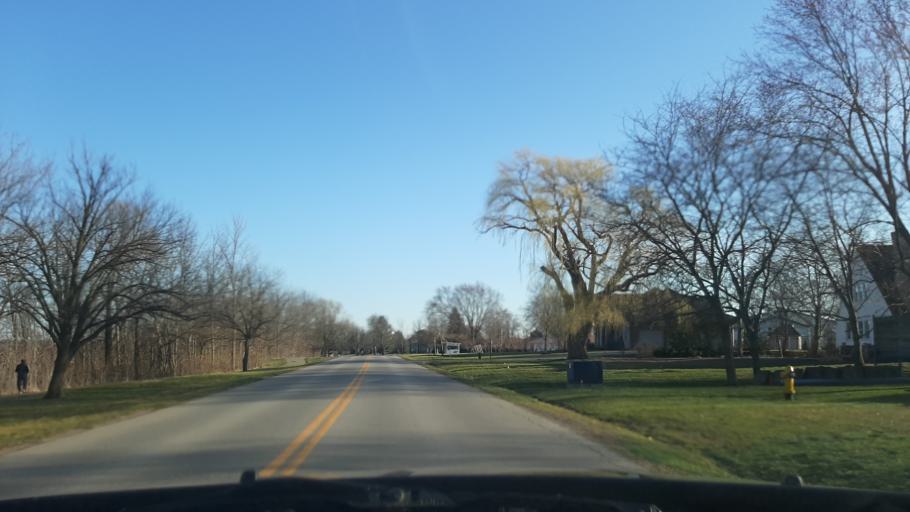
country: US
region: New York
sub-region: Niagara County
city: Youngstown
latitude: 43.2099
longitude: -79.0612
